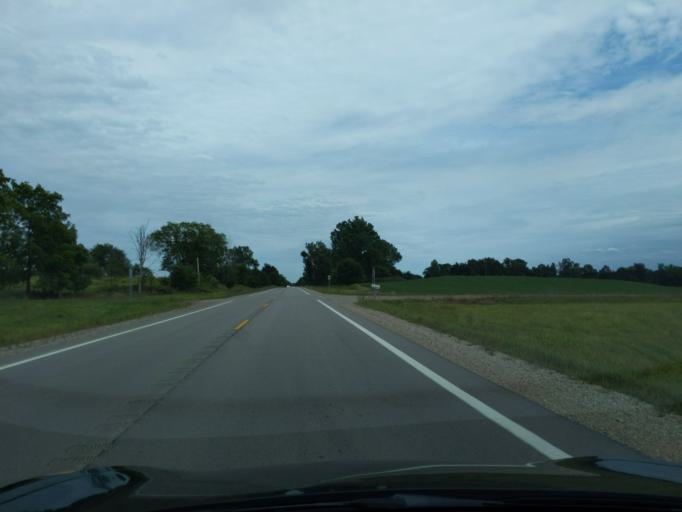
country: US
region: Michigan
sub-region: Barry County
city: Nashville
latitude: 42.5673
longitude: -85.0346
